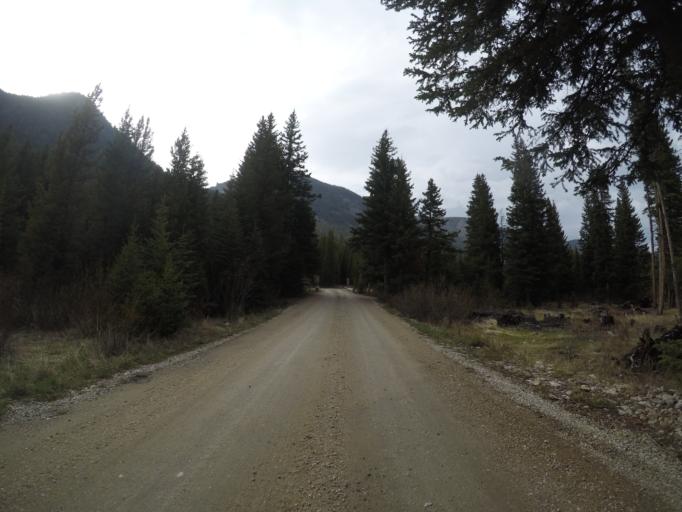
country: US
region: Montana
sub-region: Carbon County
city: Red Lodge
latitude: 45.0414
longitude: -109.4272
